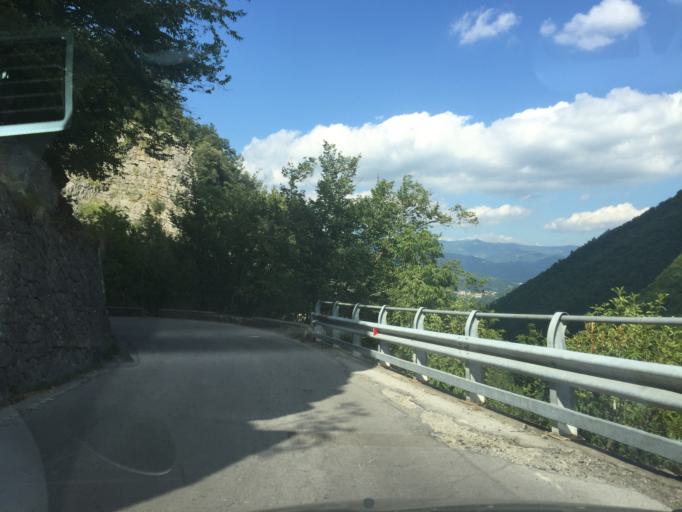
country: IT
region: Tuscany
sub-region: Provincia di Lucca
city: Careggine
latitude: 44.1294
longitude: 10.3056
